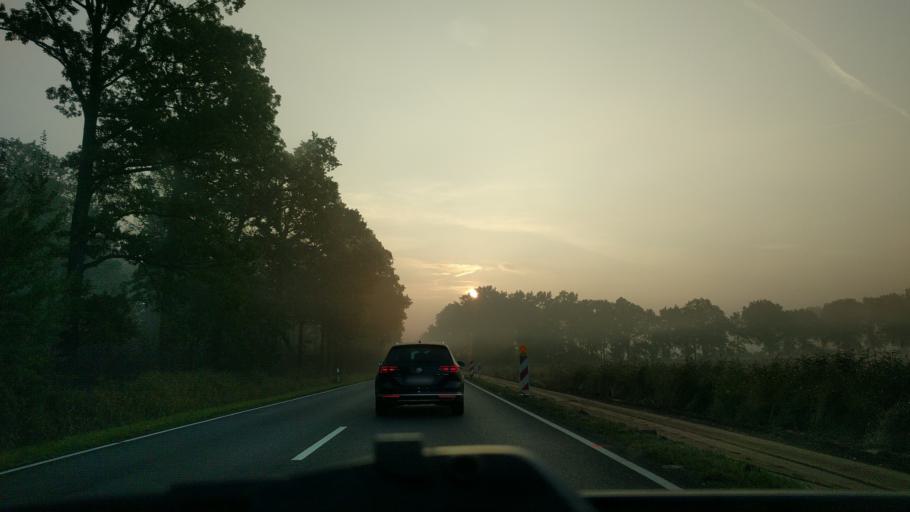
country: DE
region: Lower Saxony
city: Calberlah
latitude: 52.4312
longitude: 10.6374
